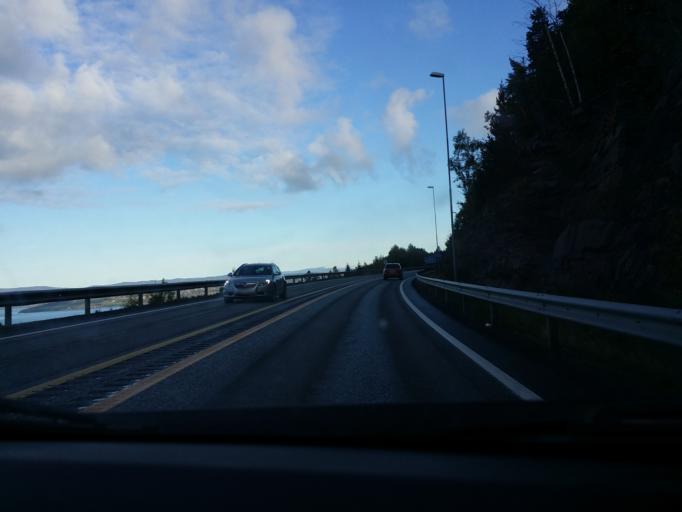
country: NO
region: Buskerud
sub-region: Hole
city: Vik
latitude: 60.0136
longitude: 10.2697
